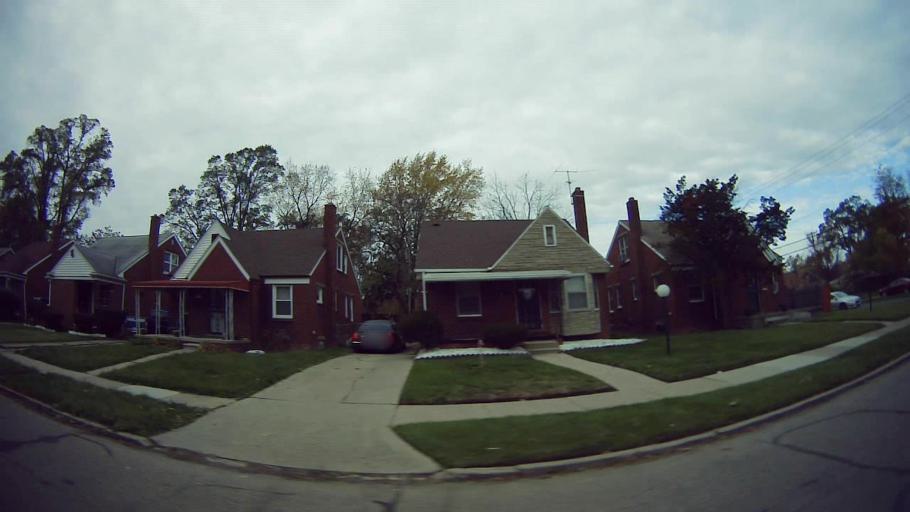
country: US
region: Michigan
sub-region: Wayne County
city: Dearborn
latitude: 42.3678
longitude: -83.1876
